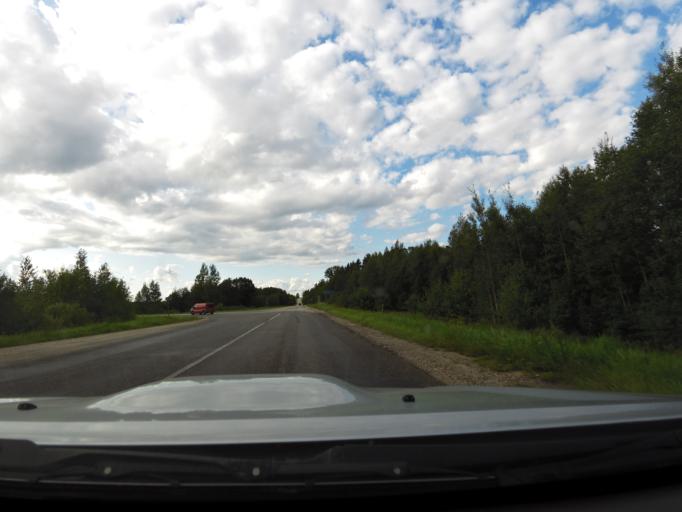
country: LV
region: Akniste
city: Akniste
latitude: 56.0221
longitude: 25.9207
